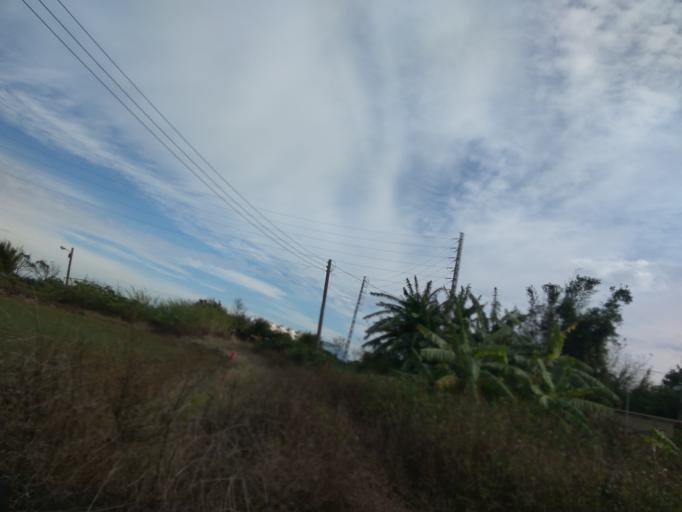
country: TW
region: Taiwan
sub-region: Hsinchu
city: Zhubei
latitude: 24.9846
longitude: 121.0909
